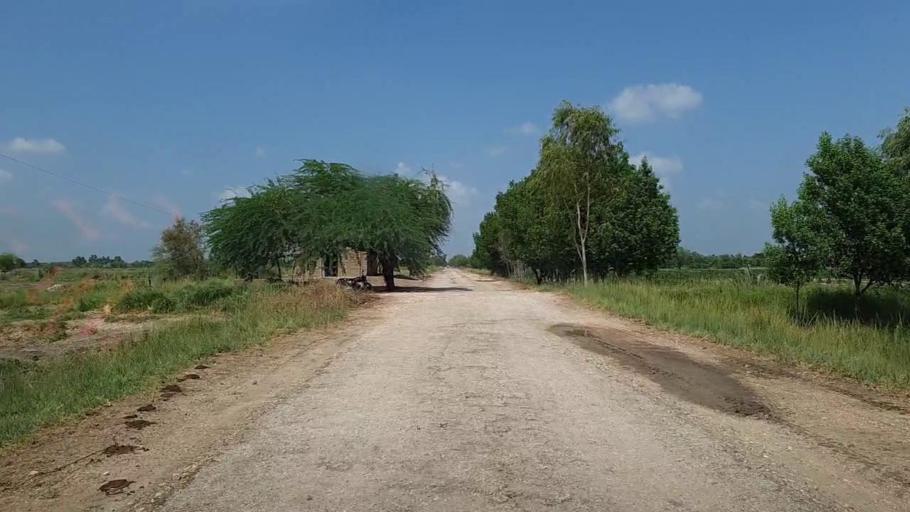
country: PK
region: Sindh
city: Kandiaro
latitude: 27.0165
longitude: 68.2677
